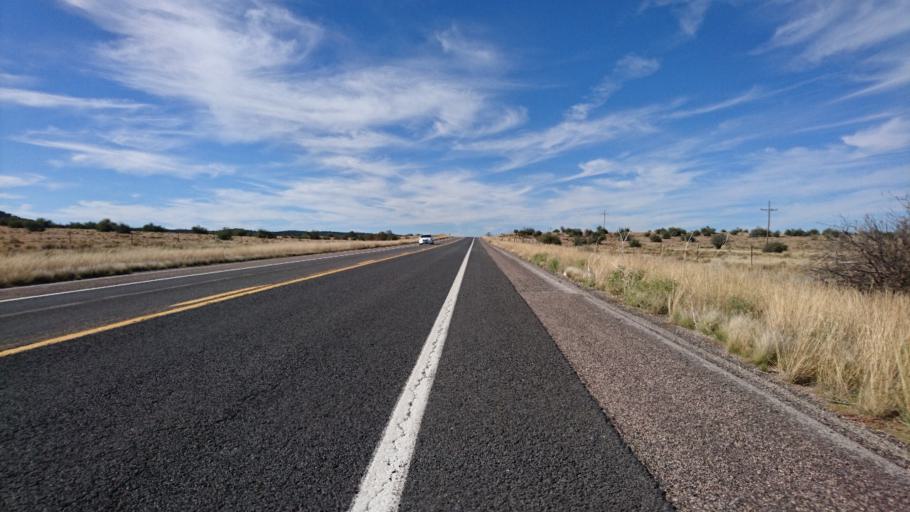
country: US
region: Arizona
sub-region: Mohave County
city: Peach Springs
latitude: 35.4926
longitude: -113.1600
